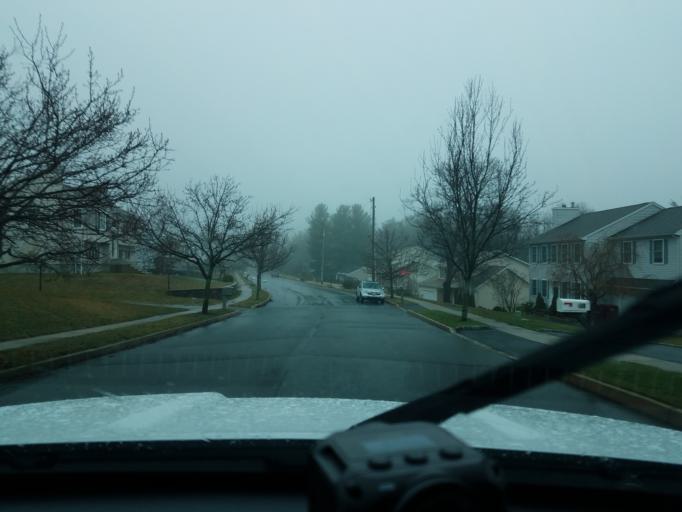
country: US
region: Connecticut
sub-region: New Haven County
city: Naugatuck
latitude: 41.4996
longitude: -73.0332
